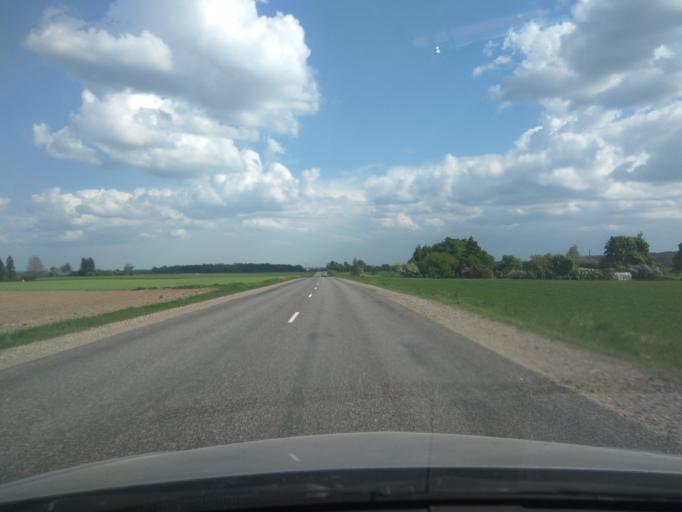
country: LV
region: Kuldigas Rajons
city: Kuldiga
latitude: 56.9950
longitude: 21.9056
